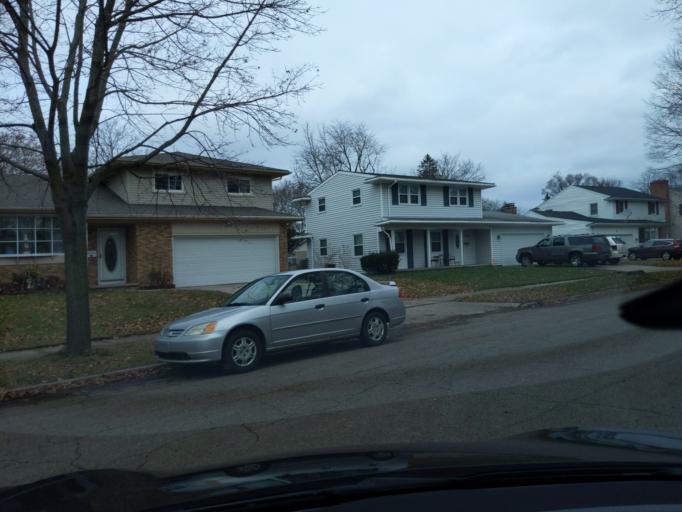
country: US
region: Michigan
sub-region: Ingham County
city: Lansing
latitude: 42.7086
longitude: -84.5846
